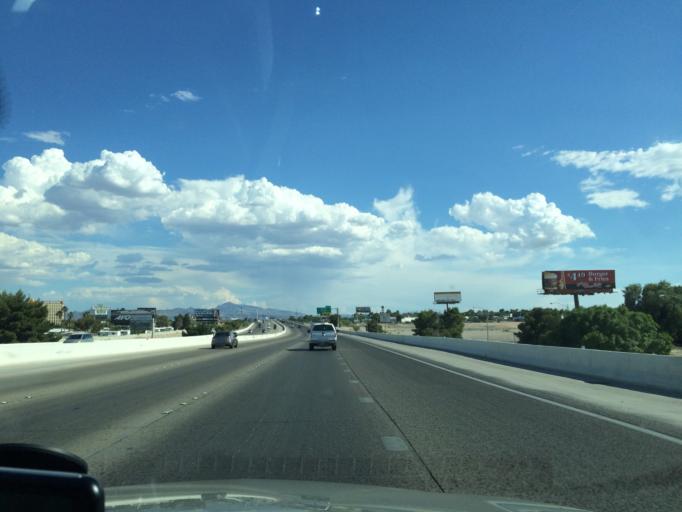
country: US
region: Nevada
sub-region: Clark County
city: Winchester
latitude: 36.1440
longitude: -115.0914
